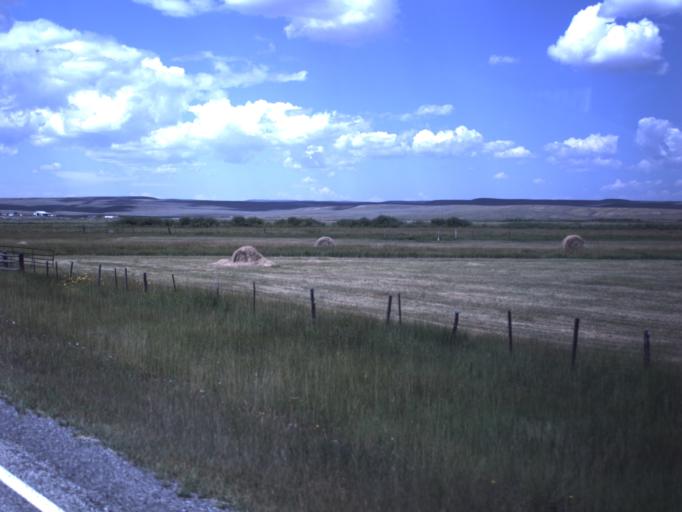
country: US
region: Utah
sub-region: Rich County
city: Randolph
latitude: 41.7748
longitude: -111.0985
